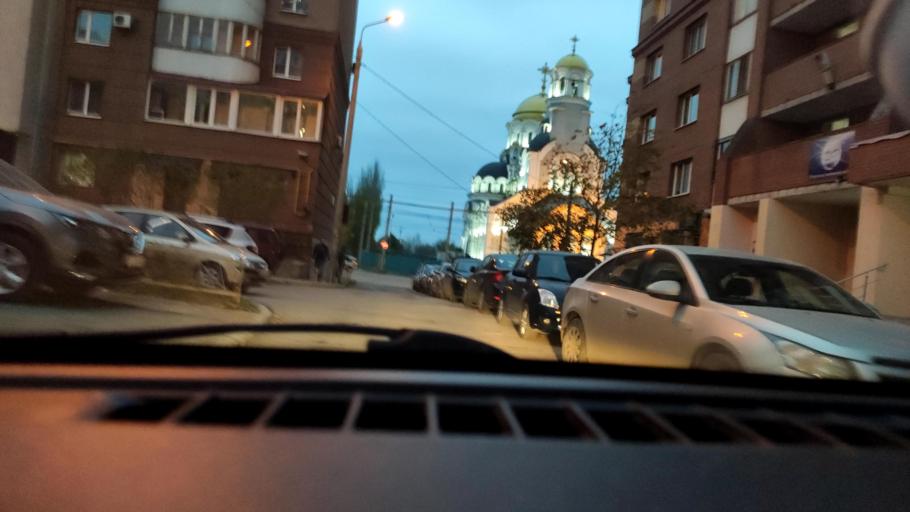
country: RU
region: Samara
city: Samara
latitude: 53.1971
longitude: 50.1546
